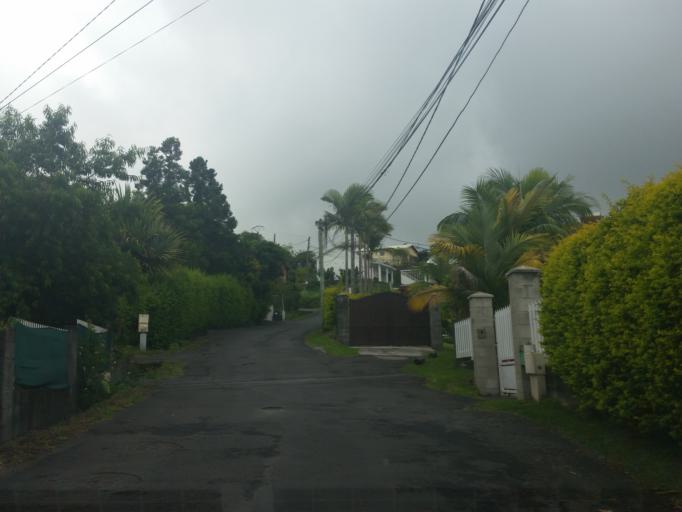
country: RE
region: Reunion
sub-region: Reunion
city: Le Tampon
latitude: -21.2372
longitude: 55.5194
